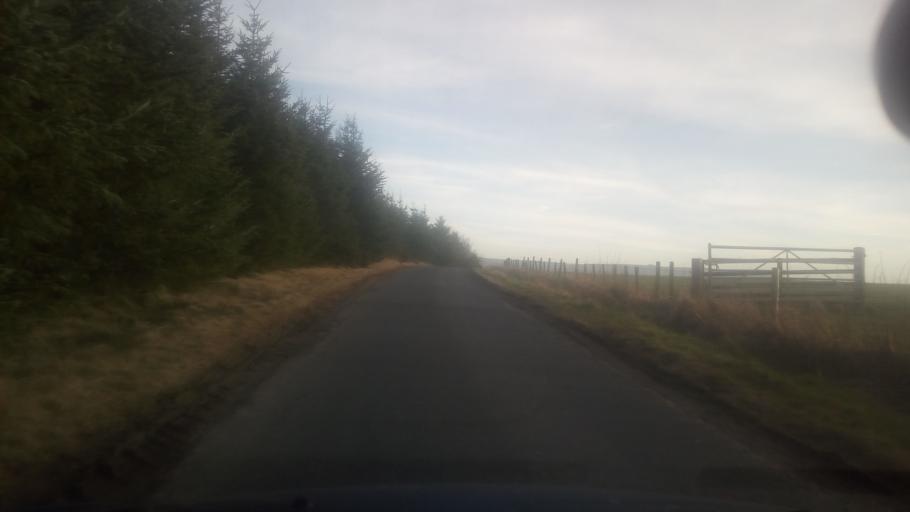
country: GB
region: Scotland
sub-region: The Scottish Borders
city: Jedburgh
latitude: 55.3994
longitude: -2.5957
